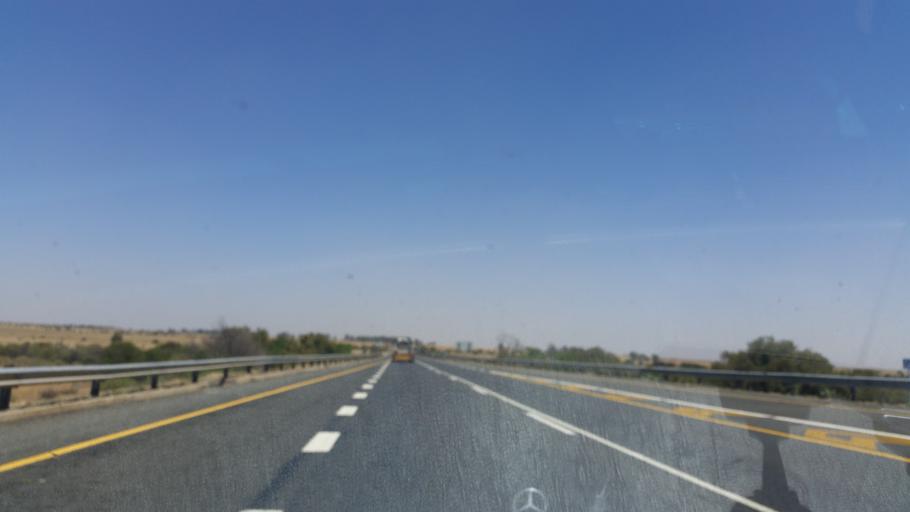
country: ZA
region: Orange Free State
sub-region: Lejweleputswa District Municipality
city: Winburg
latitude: -28.6301
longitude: 26.9059
